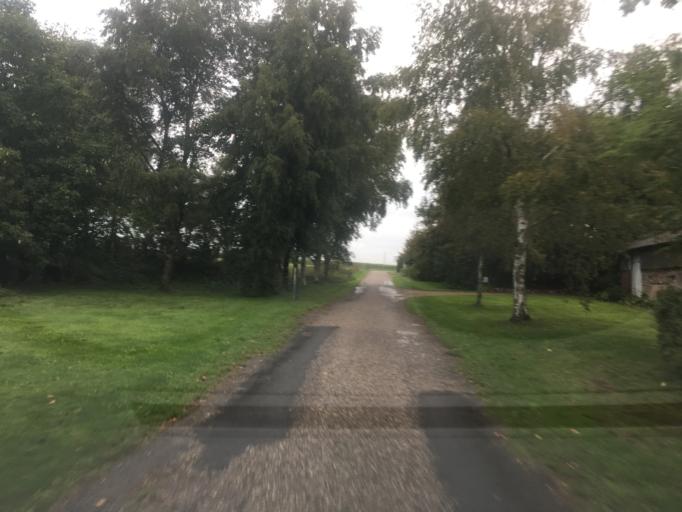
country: DK
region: South Denmark
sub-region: Tonder Kommune
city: Tonder
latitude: 54.9583
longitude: 8.8993
